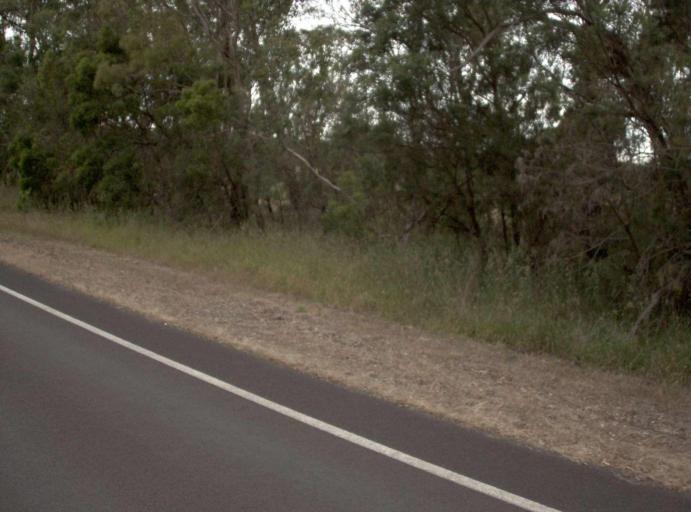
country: AU
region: Victoria
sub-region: Wellington
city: Sale
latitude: -38.4163
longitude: 146.9604
